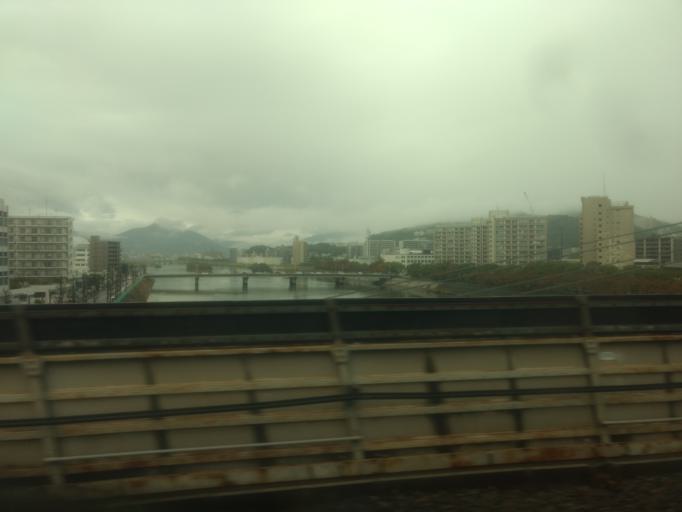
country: JP
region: Hiroshima
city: Hiroshima-shi
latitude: 34.4093
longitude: 132.4588
